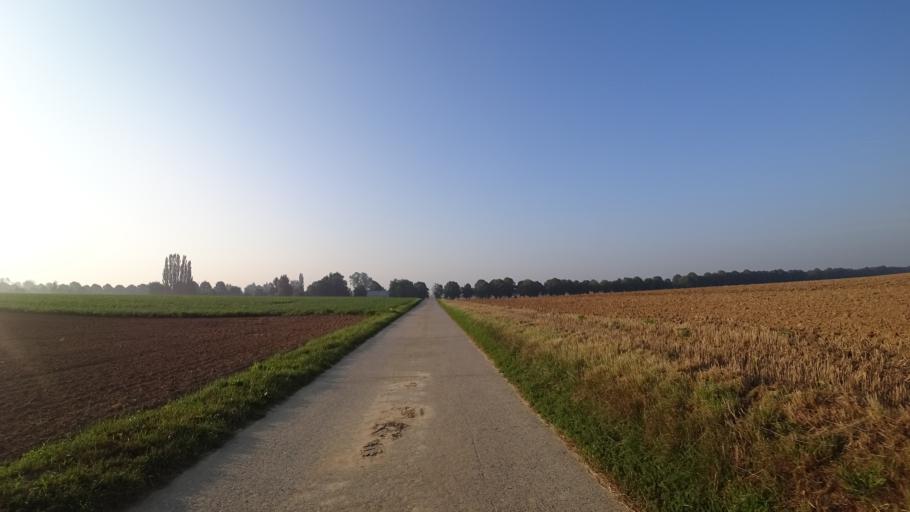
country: BE
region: Wallonia
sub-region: Province du Brabant Wallon
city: Walhain-Saint-Paul
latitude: 50.6175
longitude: 4.6809
